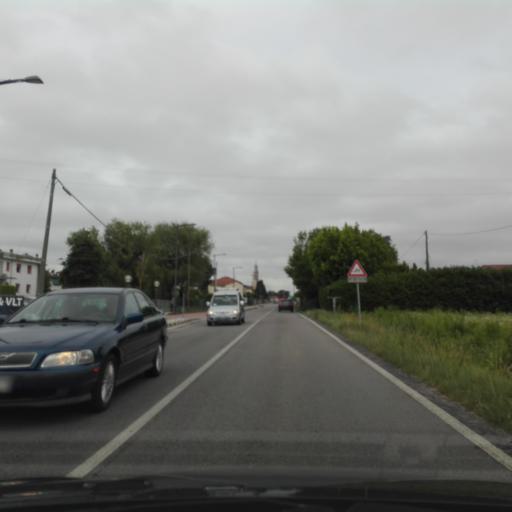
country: IT
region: Veneto
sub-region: Provincia di Rovigo
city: Lendinara
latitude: 45.0812
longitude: 11.6176
